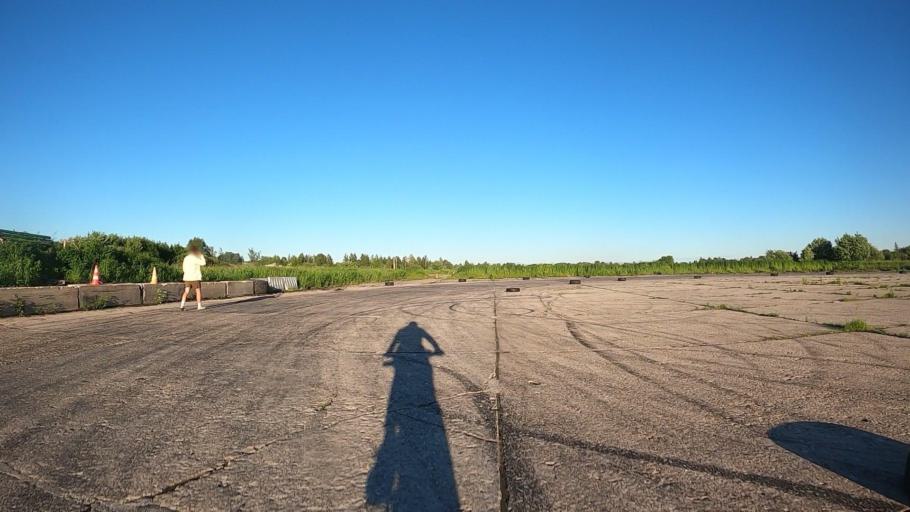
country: LV
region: Kekava
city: Kekava
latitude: 56.8813
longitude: 24.2317
